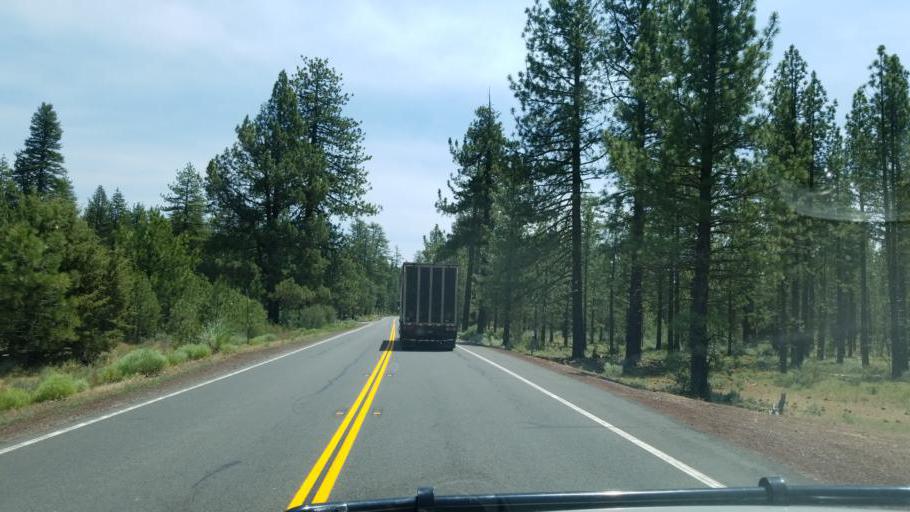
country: US
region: California
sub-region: Shasta County
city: Burney
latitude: 40.6716
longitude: -121.3645
